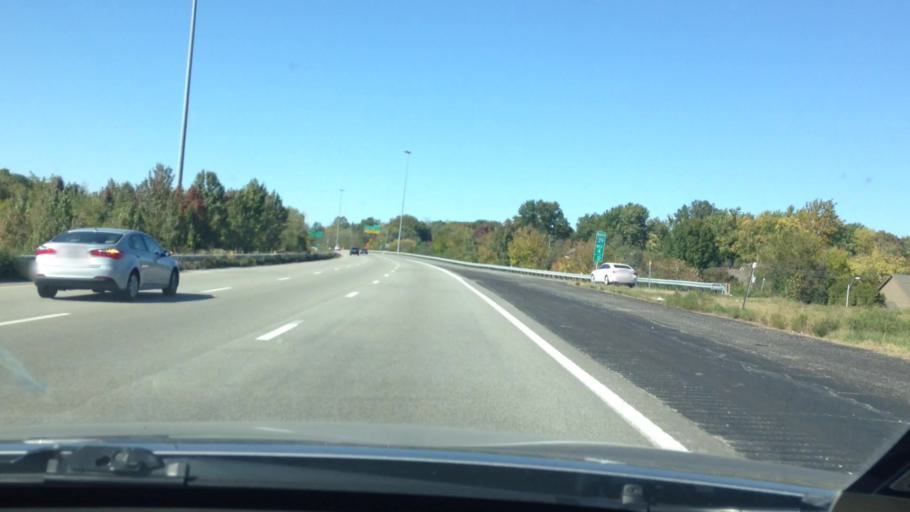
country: US
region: Missouri
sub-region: Platte County
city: Riverside
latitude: 39.1934
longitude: -94.6169
